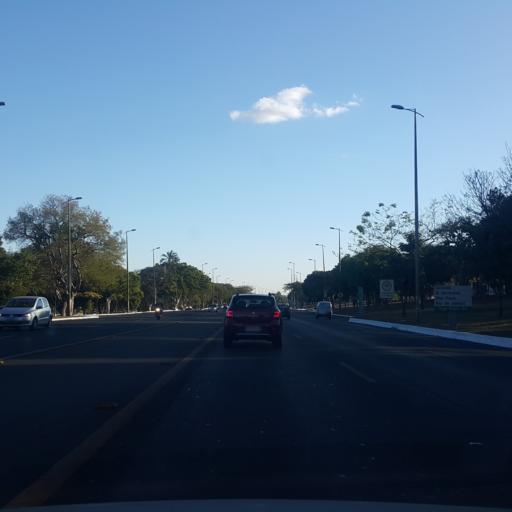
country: BR
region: Federal District
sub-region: Brasilia
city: Brasilia
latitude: -15.8114
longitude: -47.8943
